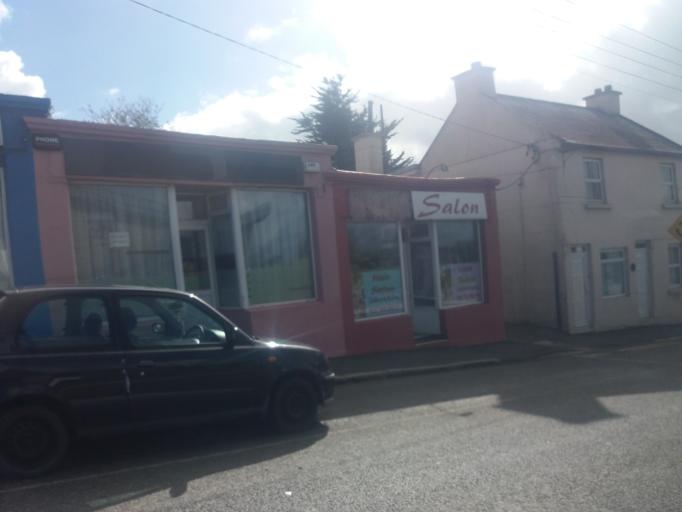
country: IE
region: Leinster
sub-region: Loch Garman
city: Ferns
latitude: 52.5906
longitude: -6.4968
